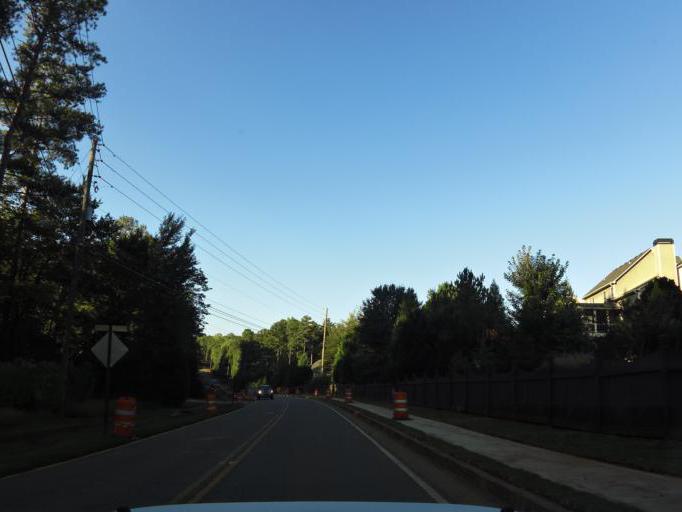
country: US
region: Georgia
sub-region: Cobb County
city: Kennesaw
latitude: 34.0048
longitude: -84.6383
